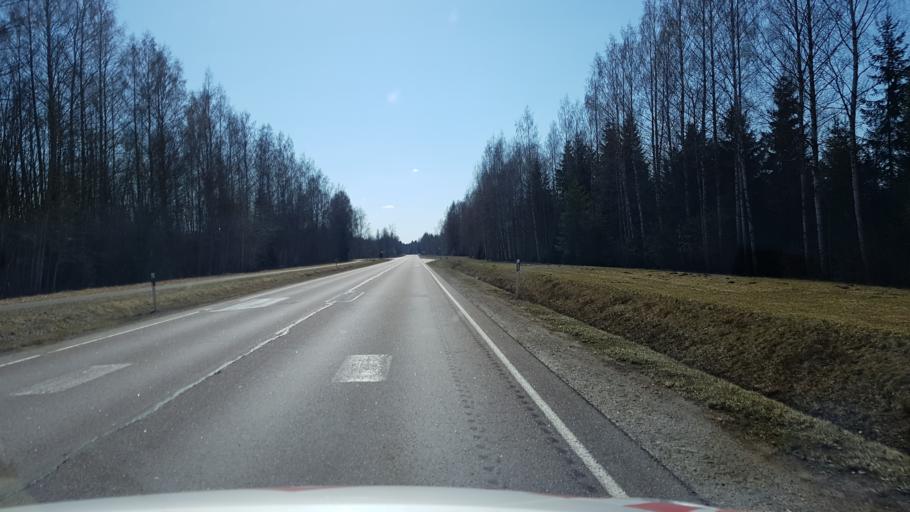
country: EE
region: Jogevamaa
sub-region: Mustvee linn
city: Mustvee
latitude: 58.7718
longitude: 26.9068
